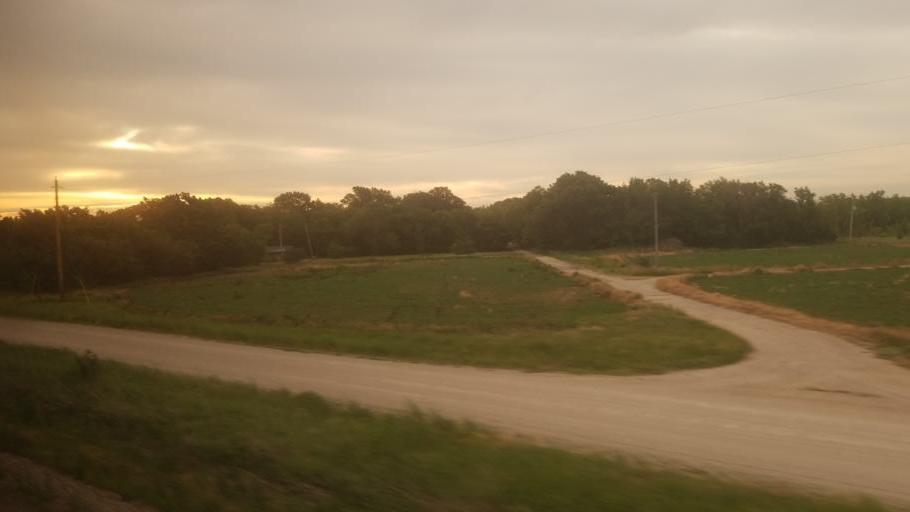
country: US
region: Kansas
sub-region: Chase County
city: Cottonwood Falls
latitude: 38.3716
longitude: -96.6496
